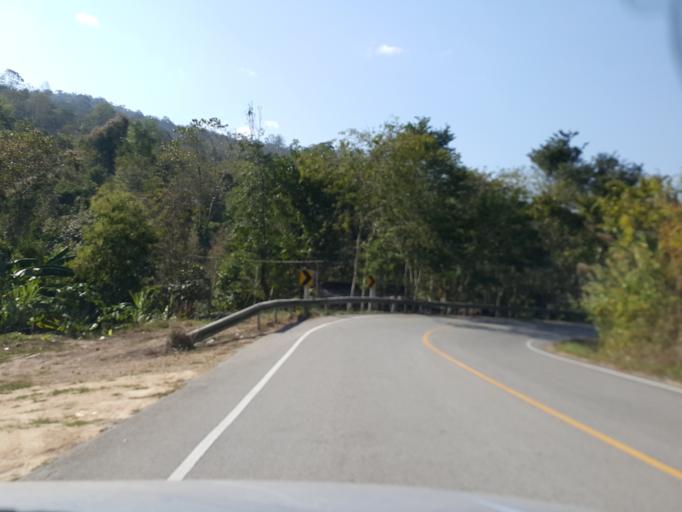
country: TH
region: Chiang Mai
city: Mae Wang
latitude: 18.6257
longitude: 98.7149
